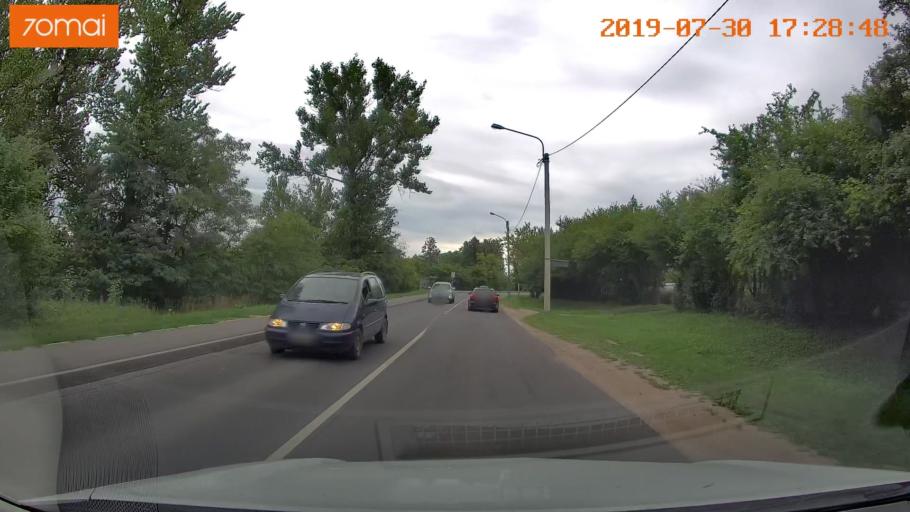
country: LT
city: Skaidiskes
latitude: 54.7028
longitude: 25.4142
